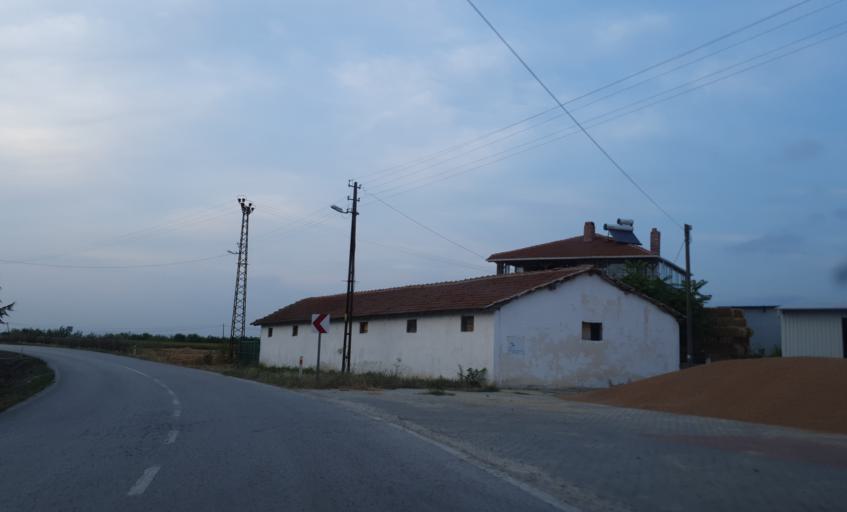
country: TR
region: Kirklareli
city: Buyukkaristiran
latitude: 41.3489
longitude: 27.6104
